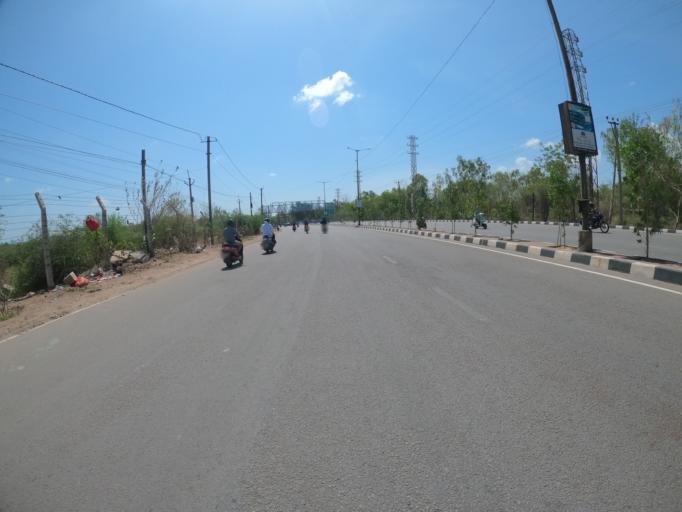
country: IN
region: Telangana
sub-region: Hyderabad
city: Hyderabad
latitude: 17.3683
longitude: 78.4018
